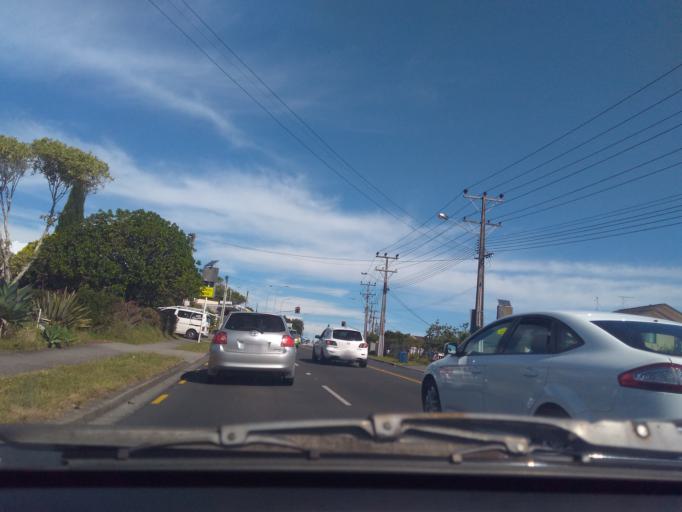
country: NZ
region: Auckland
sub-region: Auckland
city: Waitakere
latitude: -36.9065
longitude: 174.6620
